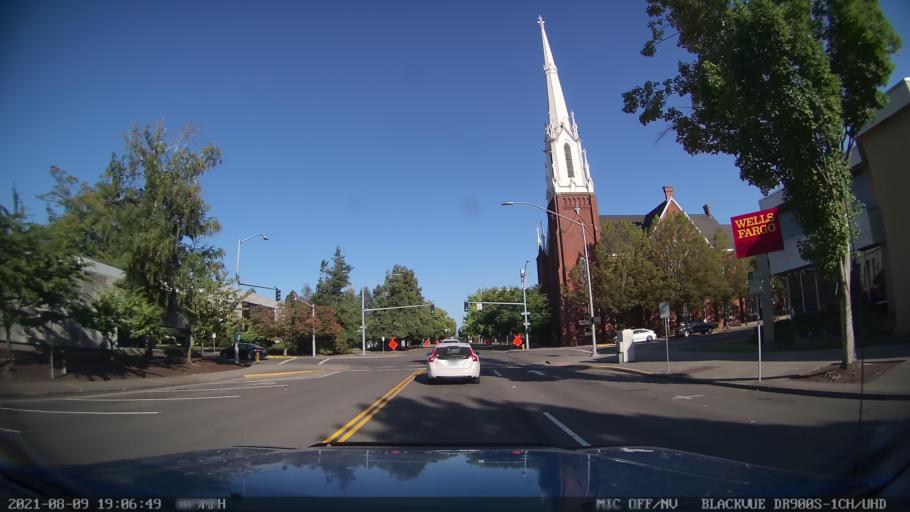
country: US
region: Oregon
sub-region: Marion County
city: Salem
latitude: 44.9392
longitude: -123.0361
